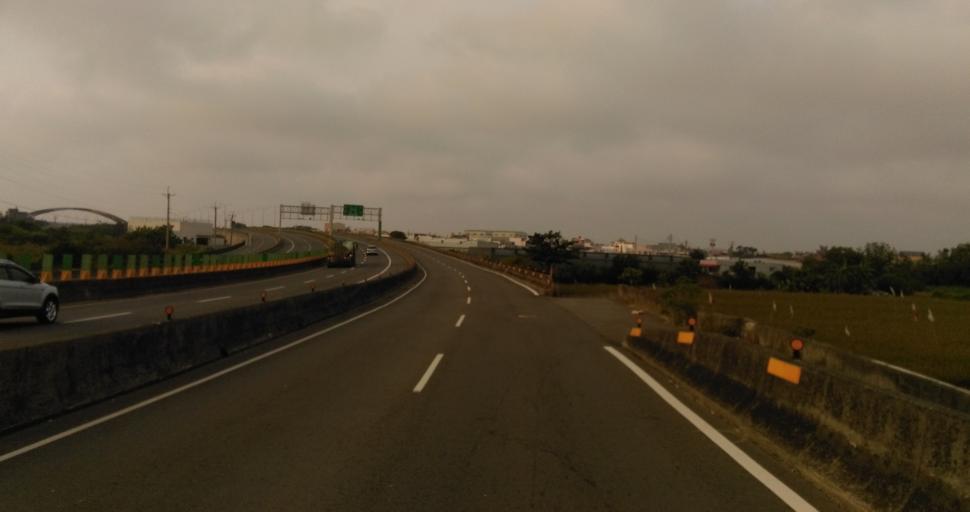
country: TW
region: Taiwan
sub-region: Hsinchu
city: Hsinchu
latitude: 24.8010
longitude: 120.9207
